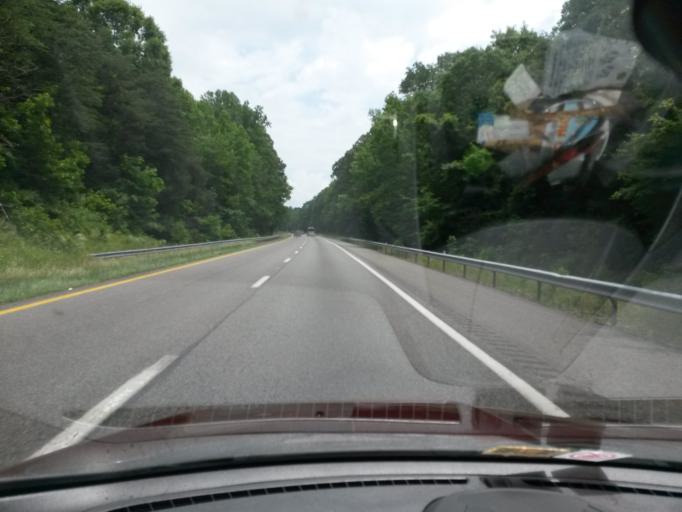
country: US
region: Virginia
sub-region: Goochland County
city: Goochland
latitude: 37.7222
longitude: -77.8166
